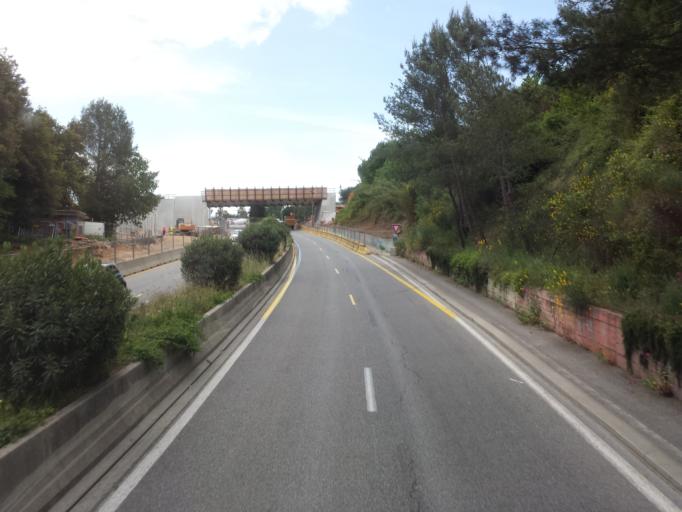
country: FR
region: Provence-Alpes-Cote d'Azur
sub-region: Departement des Alpes-Maritimes
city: Biot
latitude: 43.6066
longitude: 7.0817
